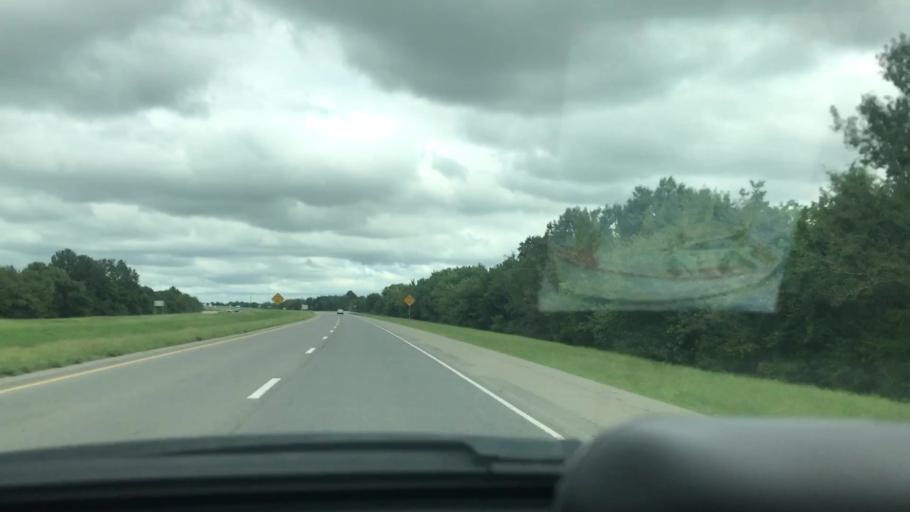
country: US
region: Oklahoma
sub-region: McIntosh County
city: Checotah
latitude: 35.5606
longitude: -95.4937
